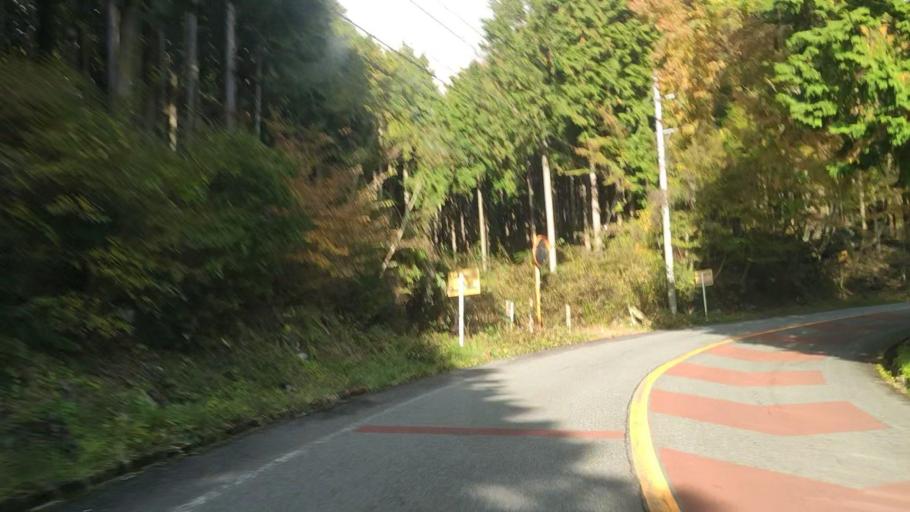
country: JP
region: Shizuoka
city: Fujinomiya
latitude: 35.2965
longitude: 138.6641
